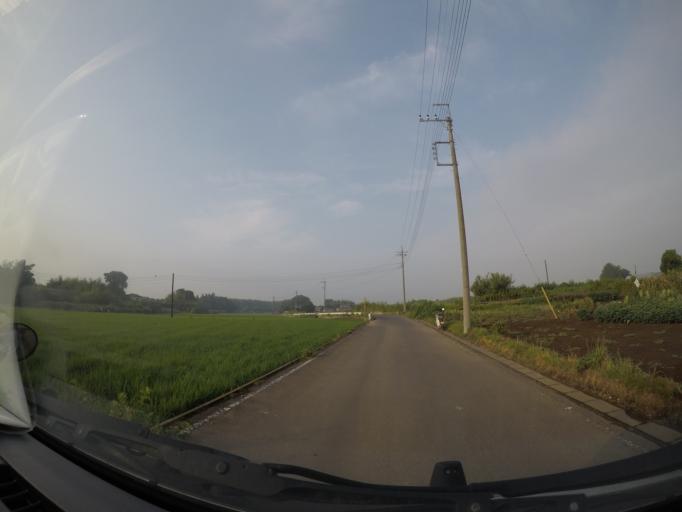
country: JP
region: Tochigi
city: Fujioka
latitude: 36.2675
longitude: 139.6771
